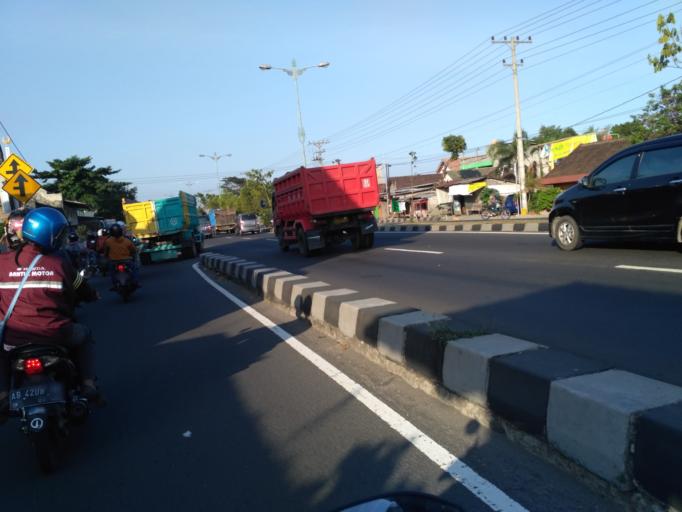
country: ID
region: Daerah Istimewa Yogyakarta
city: Sewon
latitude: -7.8354
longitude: 110.3809
